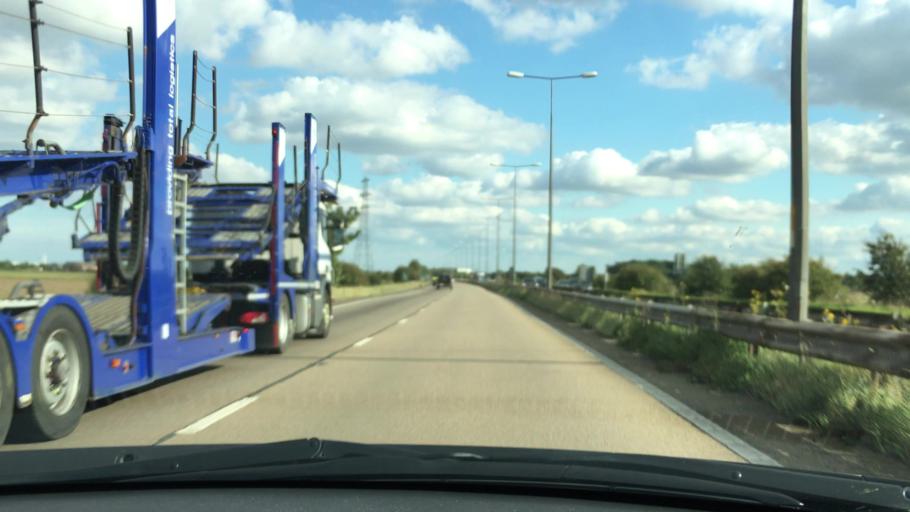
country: GB
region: England
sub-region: North East Lincolnshire
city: Healing
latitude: 53.5864
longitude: -0.1518
